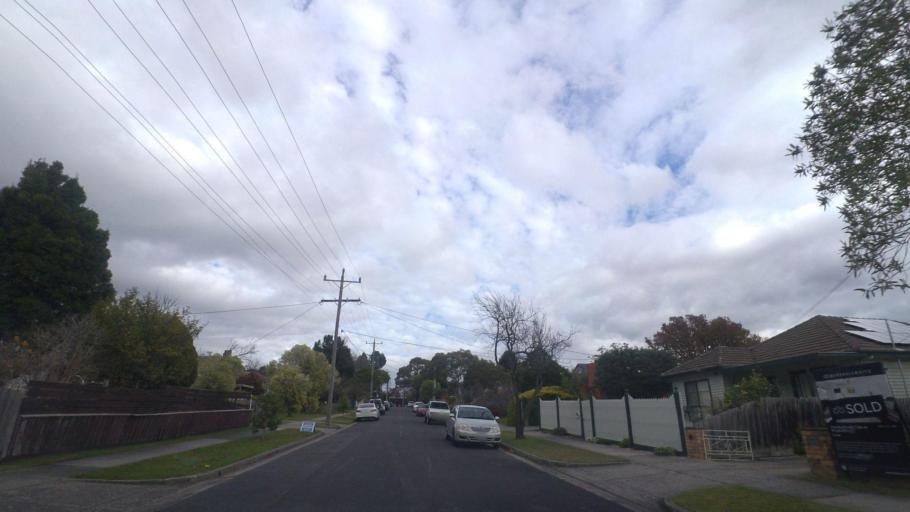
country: AU
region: Victoria
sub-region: Whitehorse
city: Nunawading
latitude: -37.8163
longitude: 145.1666
